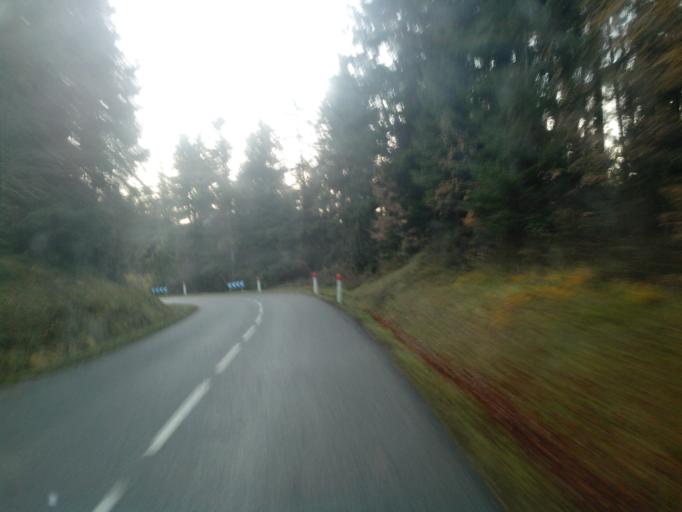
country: FR
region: Midi-Pyrenees
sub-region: Departement de l'Ariege
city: Belesta
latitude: 42.9103
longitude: 2.0028
